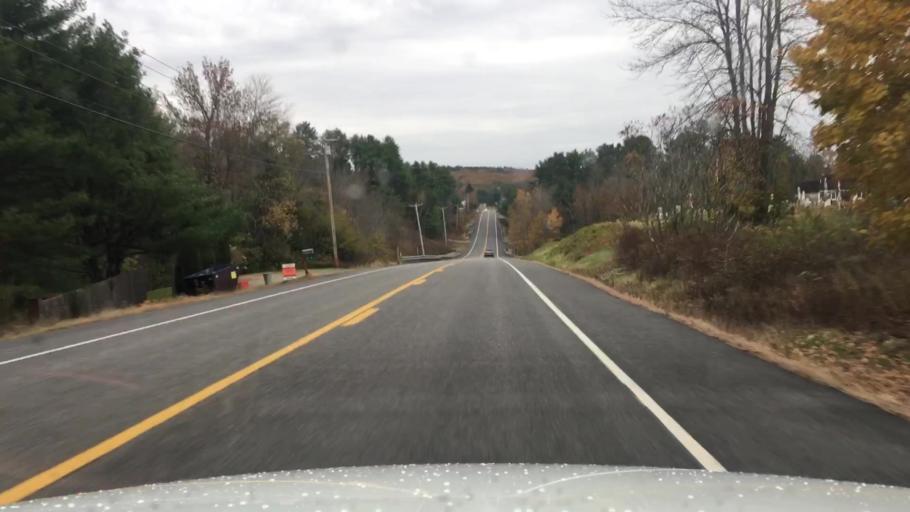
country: US
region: Maine
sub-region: Kennebec County
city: Pittston
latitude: 44.1967
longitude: -69.7516
